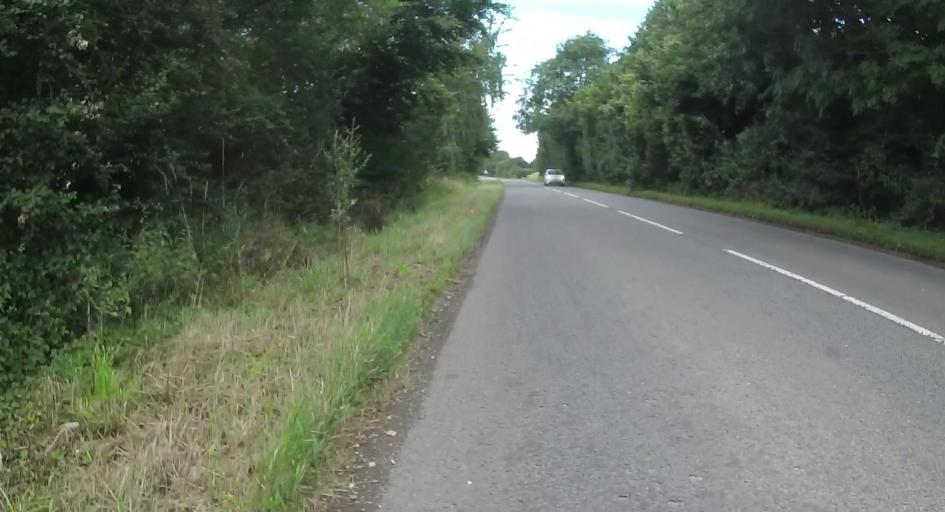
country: GB
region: England
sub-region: Hampshire
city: Overton
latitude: 51.2467
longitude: -1.3340
